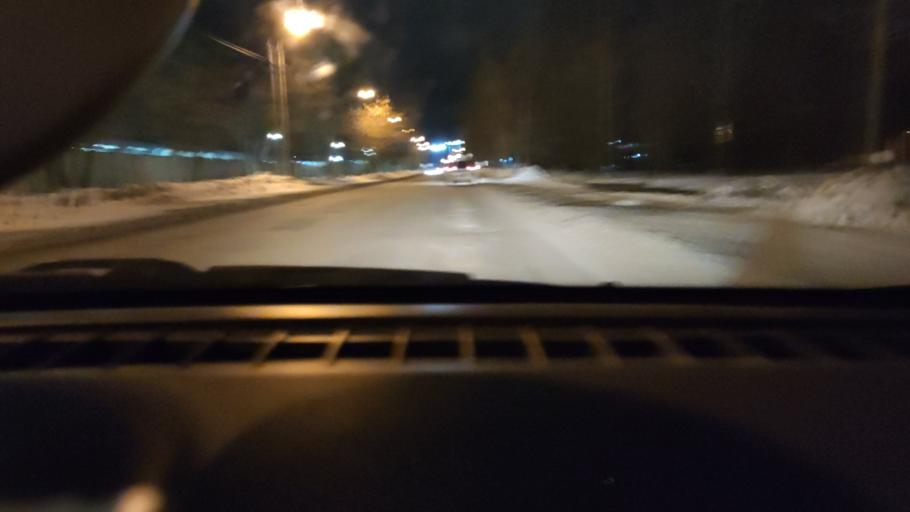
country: RU
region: Perm
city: Krasnokamsk
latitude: 58.0775
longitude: 55.7470
